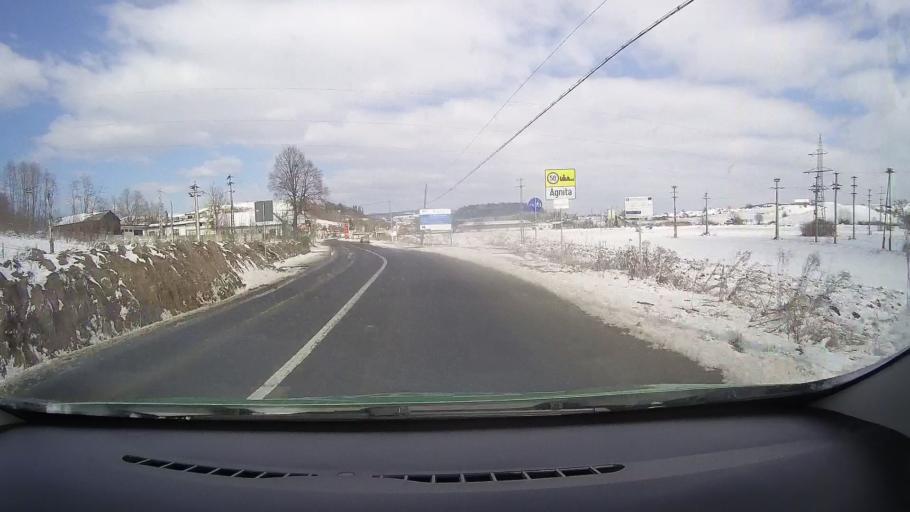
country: RO
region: Sibiu
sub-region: Oras Agnita
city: Agnita
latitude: 45.9684
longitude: 24.6042
